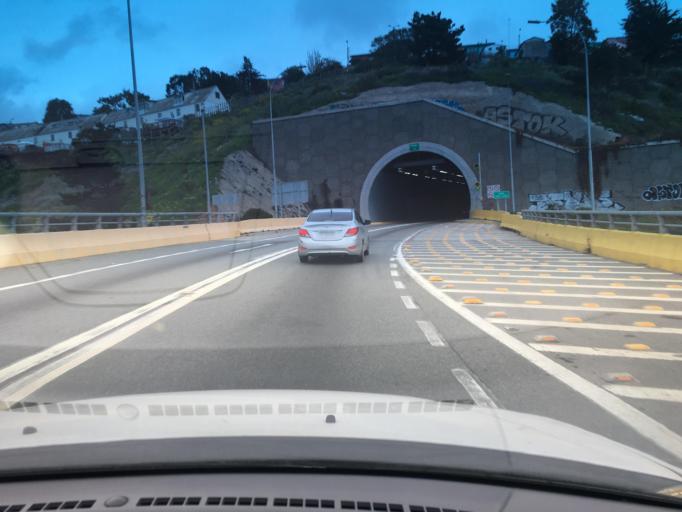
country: CL
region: Valparaiso
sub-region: Provincia de Valparaiso
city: Valparaiso
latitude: -33.0388
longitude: -71.6540
